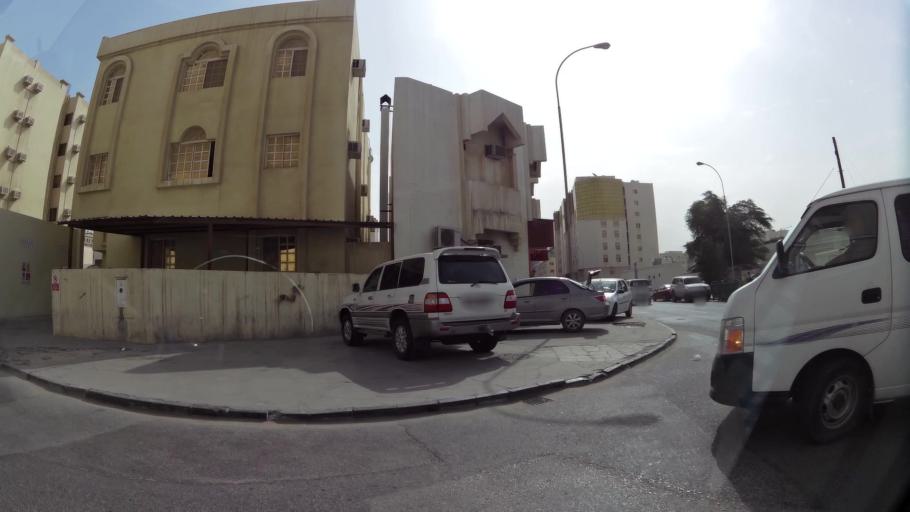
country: QA
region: Baladiyat ad Dawhah
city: Doha
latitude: 25.2850
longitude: 51.5097
